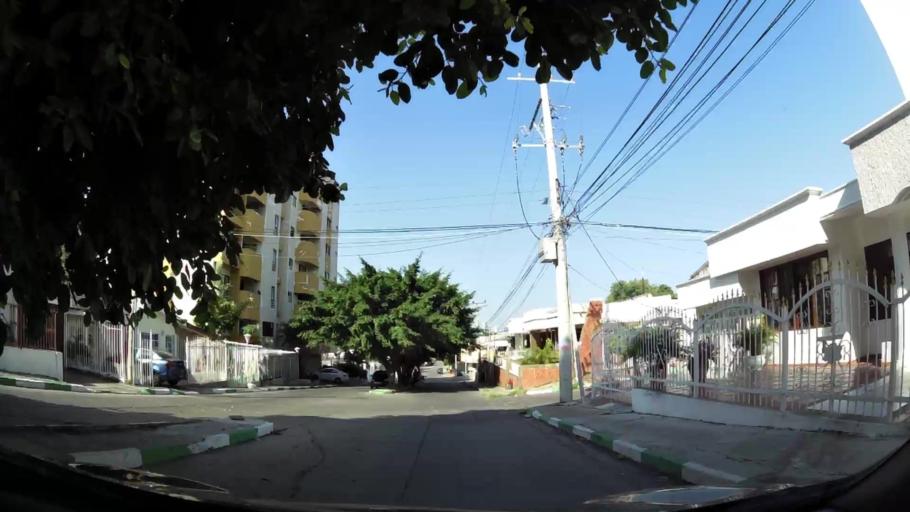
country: CO
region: Bolivar
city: Cartagena
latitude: 10.3902
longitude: -75.5181
